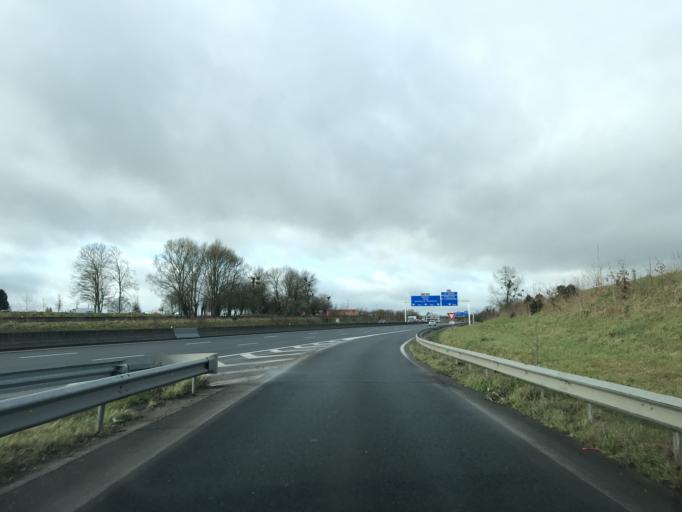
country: FR
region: Haute-Normandie
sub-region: Departement de l'Eure
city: Beuzeville
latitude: 49.3227
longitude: 0.3235
